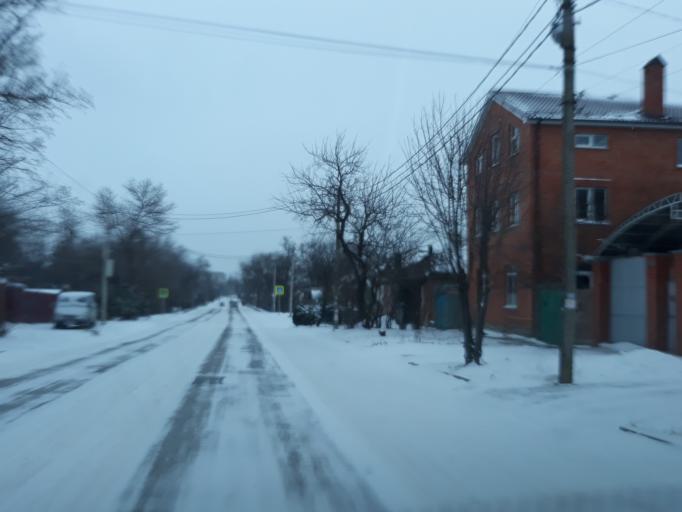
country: RU
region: Rostov
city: Taganrog
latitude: 47.2009
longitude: 38.9249
